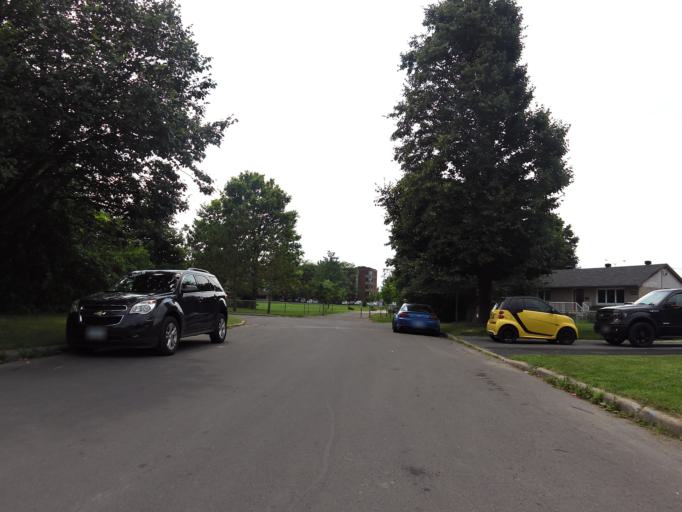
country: CA
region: Ontario
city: Bells Corners
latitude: 45.3567
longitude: -75.7750
